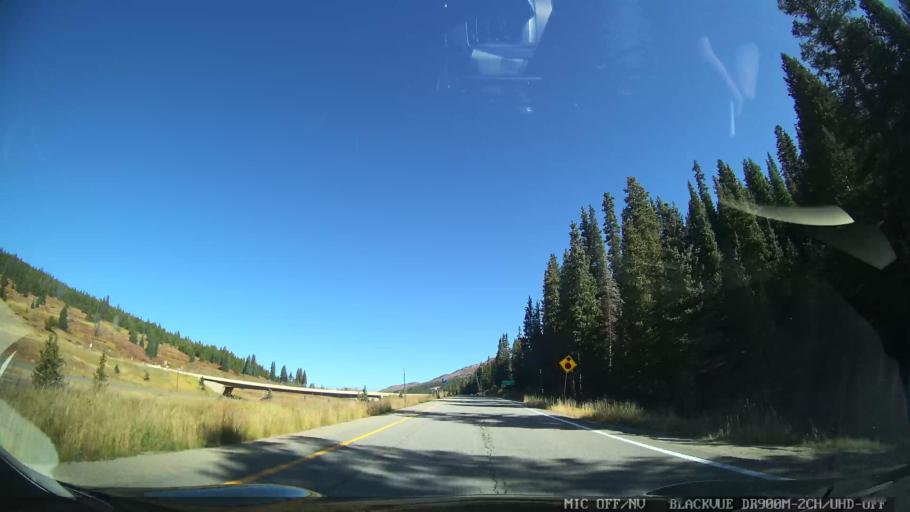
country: US
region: Colorado
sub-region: Summit County
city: Frisco
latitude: 39.5284
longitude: -106.2148
